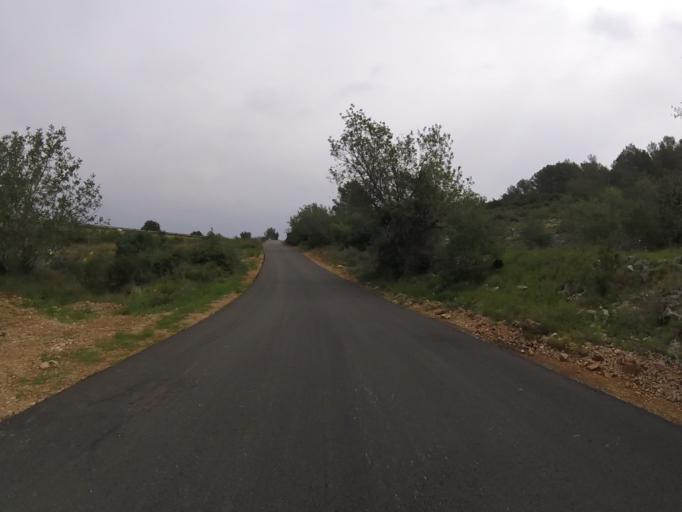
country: ES
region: Valencia
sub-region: Provincia de Castello
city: Santa Magdalena de Pulpis
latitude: 40.3532
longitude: 0.3099
